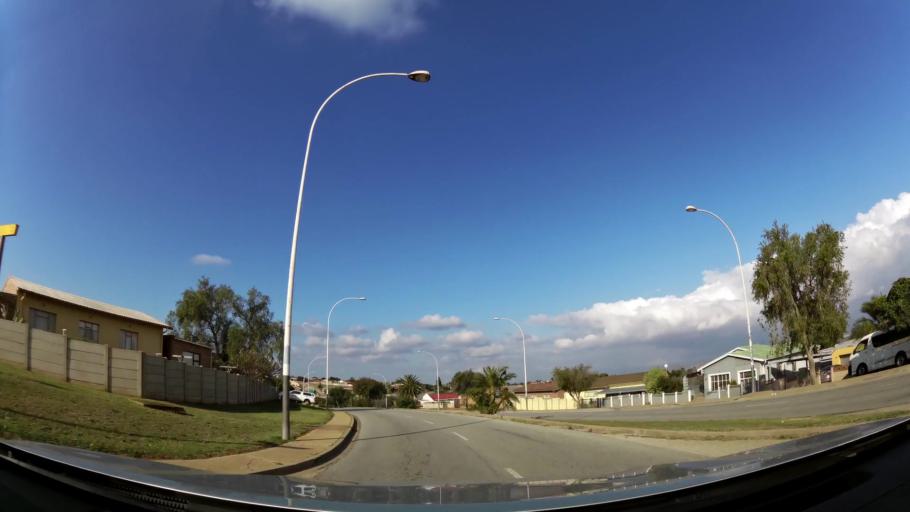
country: ZA
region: Eastern Cape
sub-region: Nelson Mandela Bay Metropolitan Municipality
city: Uitenhage
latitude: -33.7703
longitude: 25.4225
